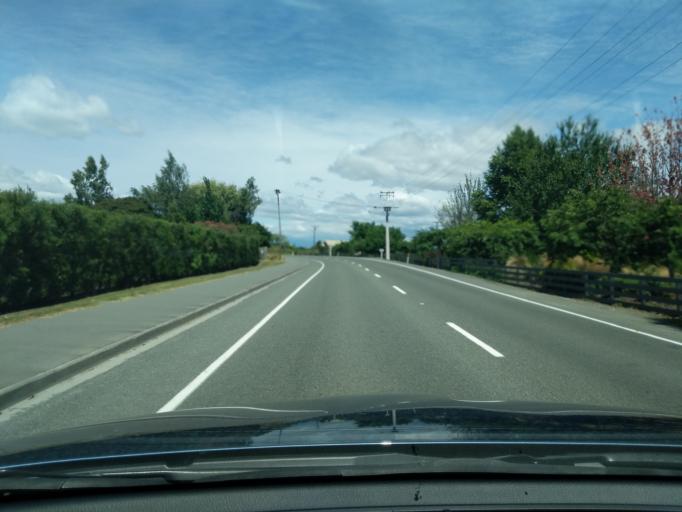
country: NZ
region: Tasman
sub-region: Tasman District
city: Motueka
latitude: -41.0968
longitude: 173.0118
